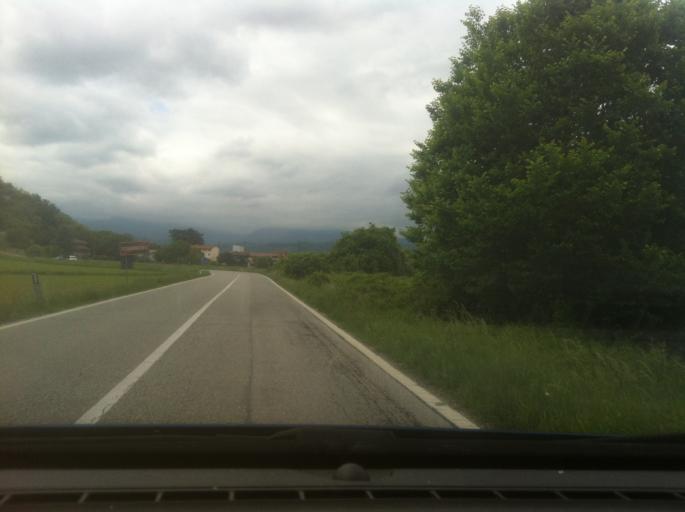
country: IT
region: Piedmont
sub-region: Provincia di Torino
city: Scarmagno
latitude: 45.3915
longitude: 7.8373
